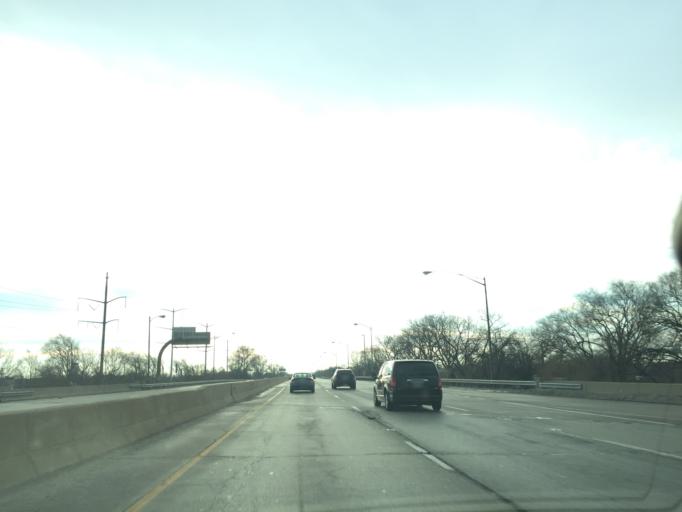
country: US
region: Illinois
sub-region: Cook County
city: Chicago
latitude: 41.7663
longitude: -87.6087
